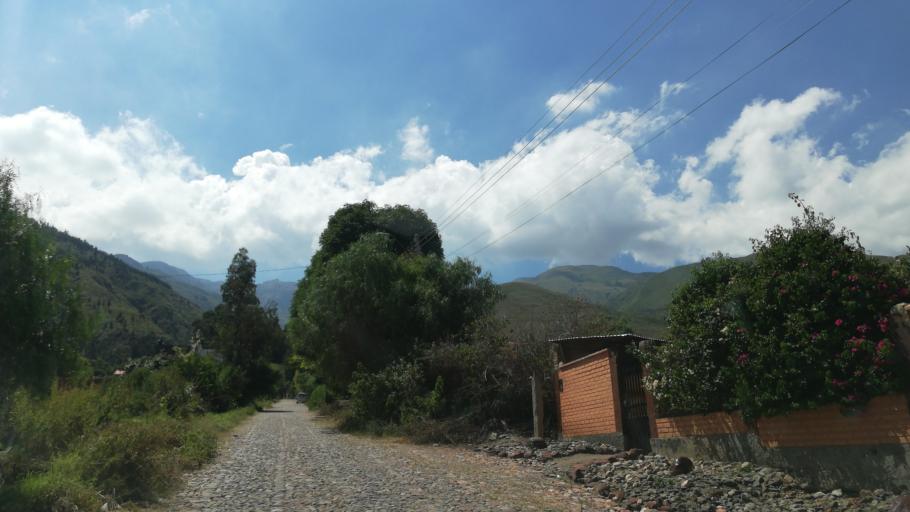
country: BO
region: Cochabamba
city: Cochabamba
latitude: -17.3242
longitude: -66.2132
